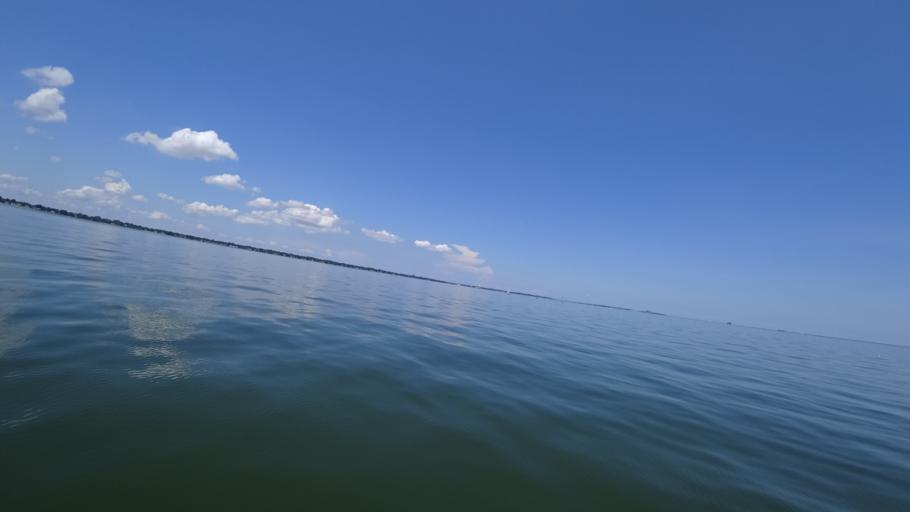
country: US
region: Virginia
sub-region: City of Newport News
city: Newport News
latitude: 36.9752
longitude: -76.3699
